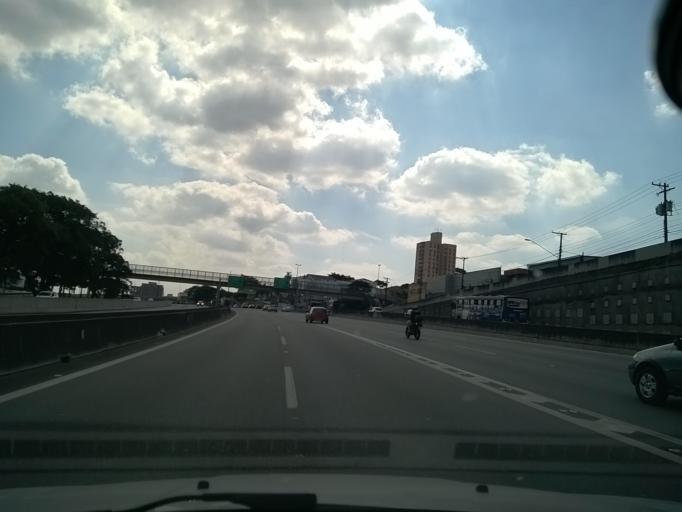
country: BR
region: Sao Paulo
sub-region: Osasco
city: Osasco
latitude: -23.5090
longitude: -46.7310
